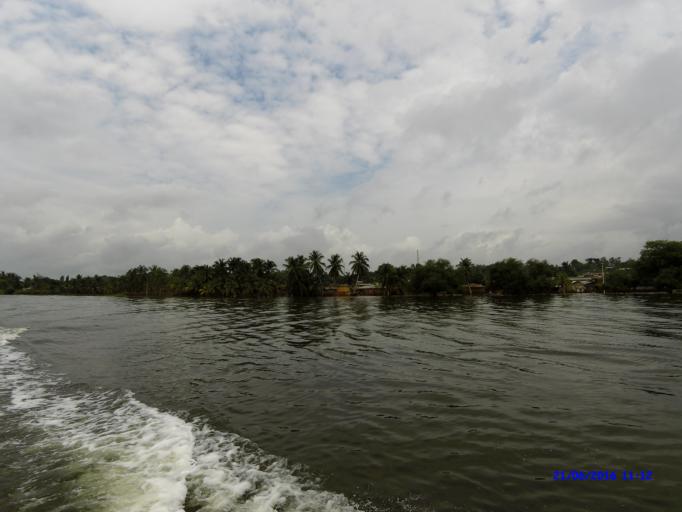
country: BJ
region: Mono
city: Come
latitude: 6.5264
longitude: 1.9709
